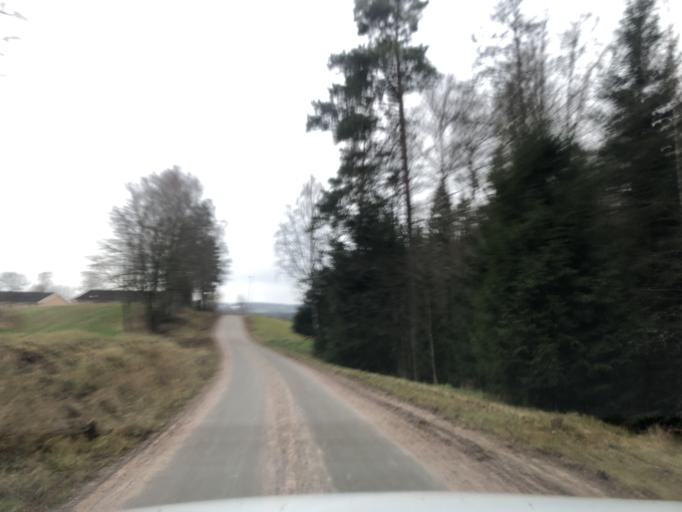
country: SE
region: Vaestra Goetaland
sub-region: Ulricehamns Kommun
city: Ulricehamn
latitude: 57.8687
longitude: 13.5563
